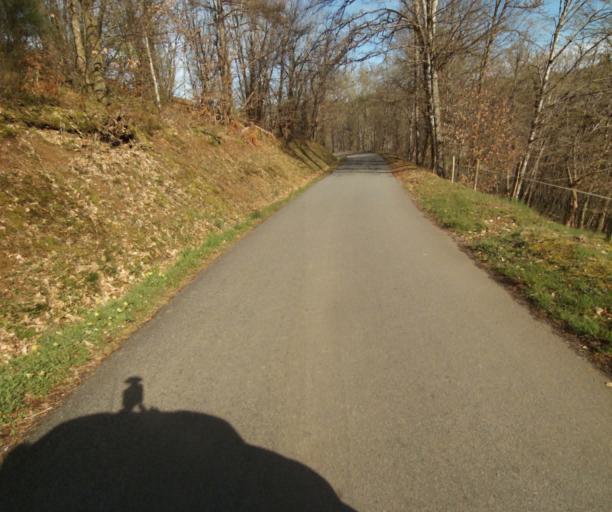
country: FR
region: Limousin
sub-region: Departement de la Correze
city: Laguenne
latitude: 45.2593
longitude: 1.8394
